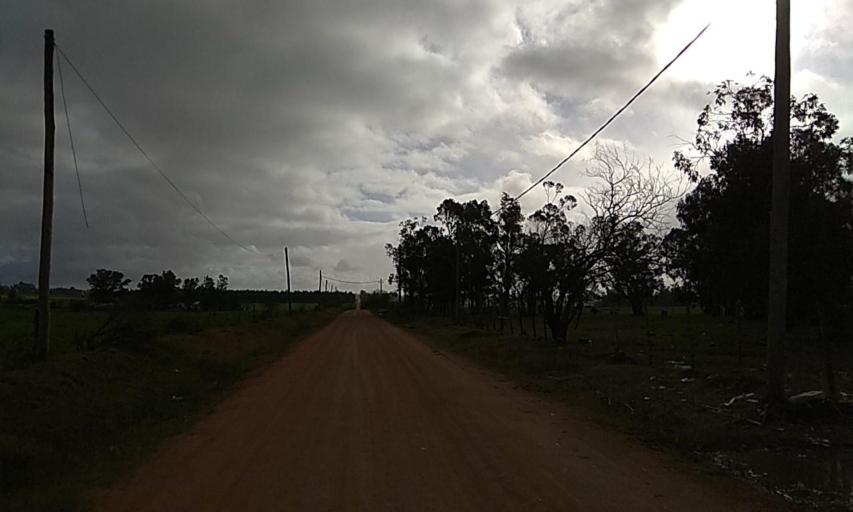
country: UY
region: Florida
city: Florida
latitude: -34.0739
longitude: -56.2333
